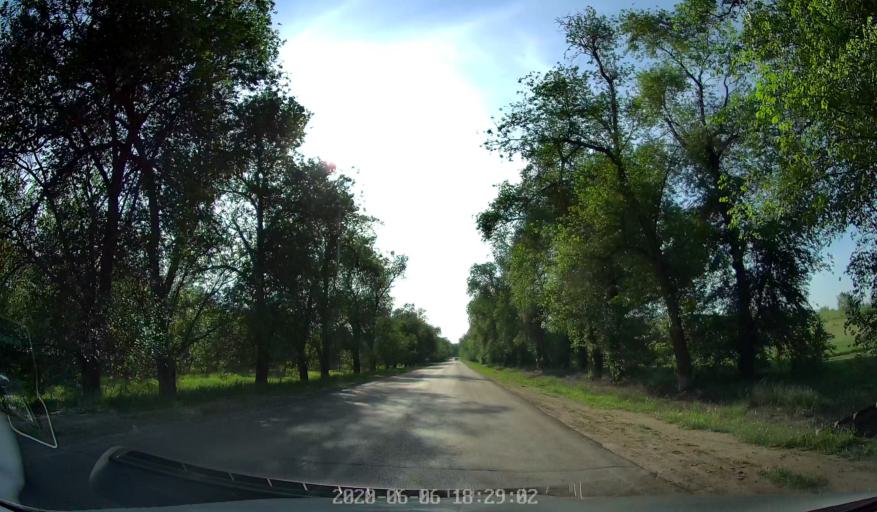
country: MD
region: Chisinau
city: Ciorescu
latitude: 47.1306
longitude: 28.9762
